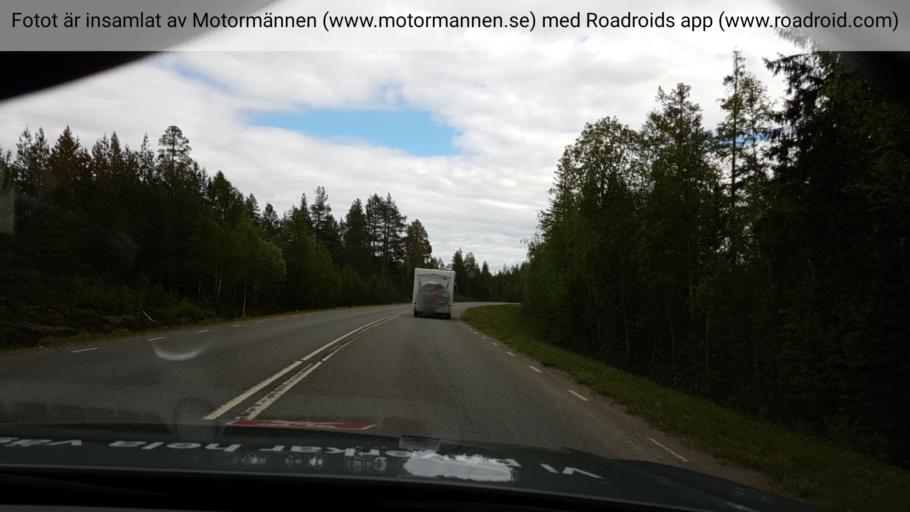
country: SE
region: Jaemtland
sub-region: Stroemsunds Kommun
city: Stroemsund
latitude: 64.3336
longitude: 15.1644
